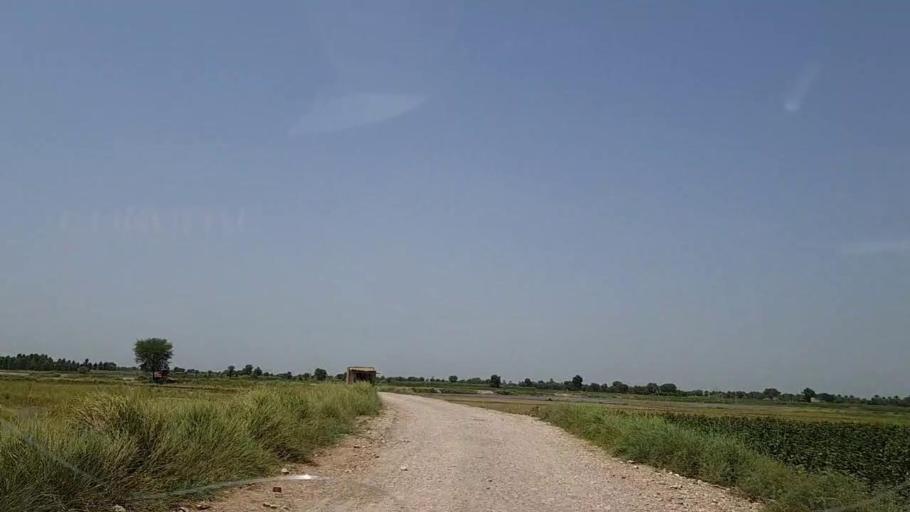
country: PK
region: Sindh
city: Tharu Shah
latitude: 26.9344
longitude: 68.0506
